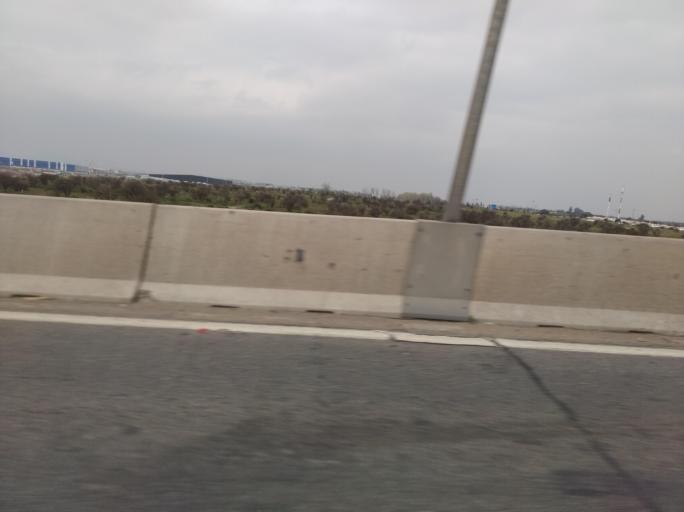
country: CL
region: Santiago Metropolitan
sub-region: Provincia de Santiago
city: Lo Prado
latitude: -33.4372
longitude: -70.8120
